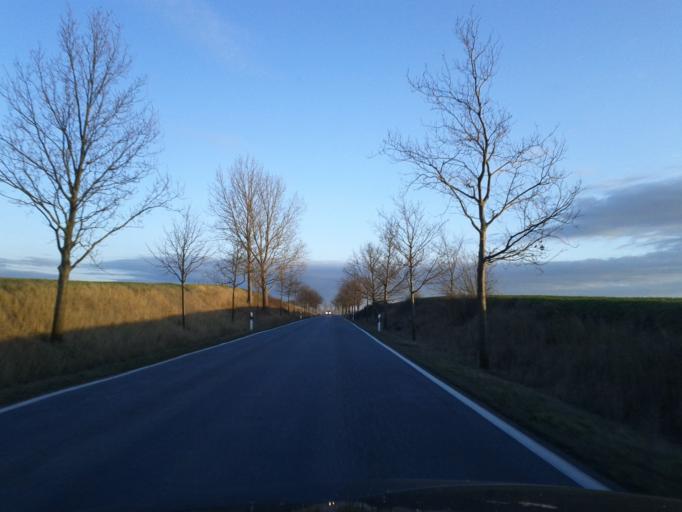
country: DE
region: Mecklenburg-Vorpommern
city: Blowatz
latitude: 53.9809
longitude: 11.4574
